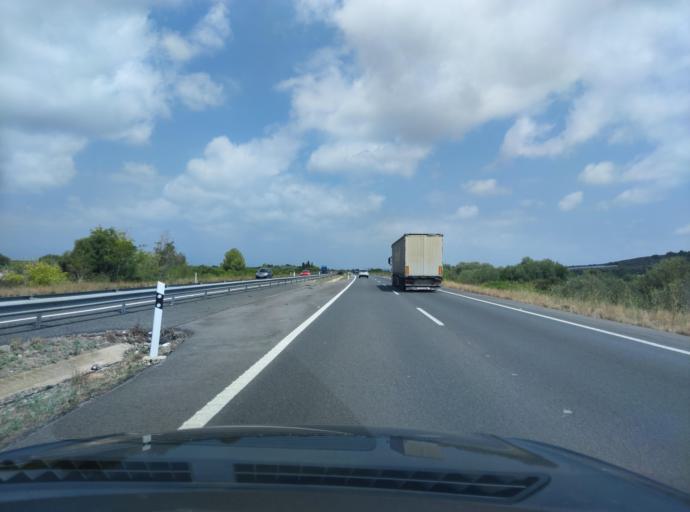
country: ES
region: Valencia
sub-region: Provincia de Castello
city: Vinaros
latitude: 40.5035
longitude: 0.4161
